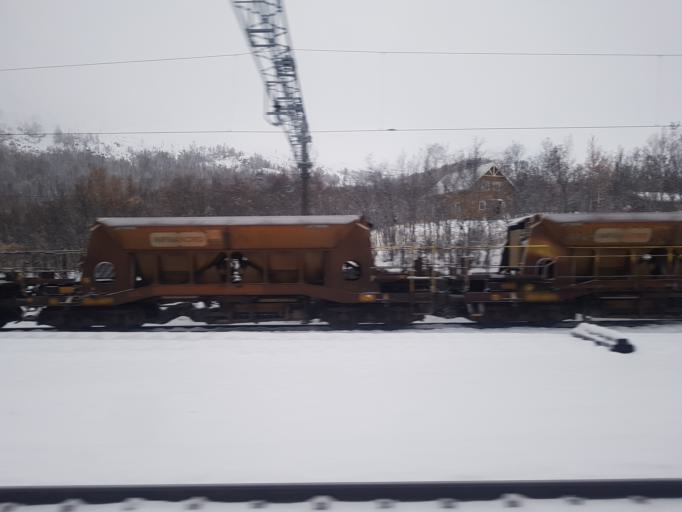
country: NO
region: Oppland
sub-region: Dovre
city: Dovre
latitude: 62.2395
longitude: 9.5324
